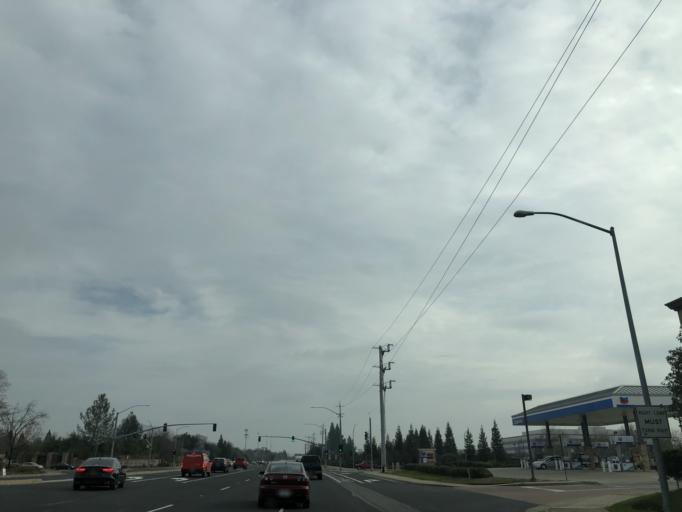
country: US
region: California
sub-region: Sacramento County
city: Folsom
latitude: 38.6504
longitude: -121.1640
